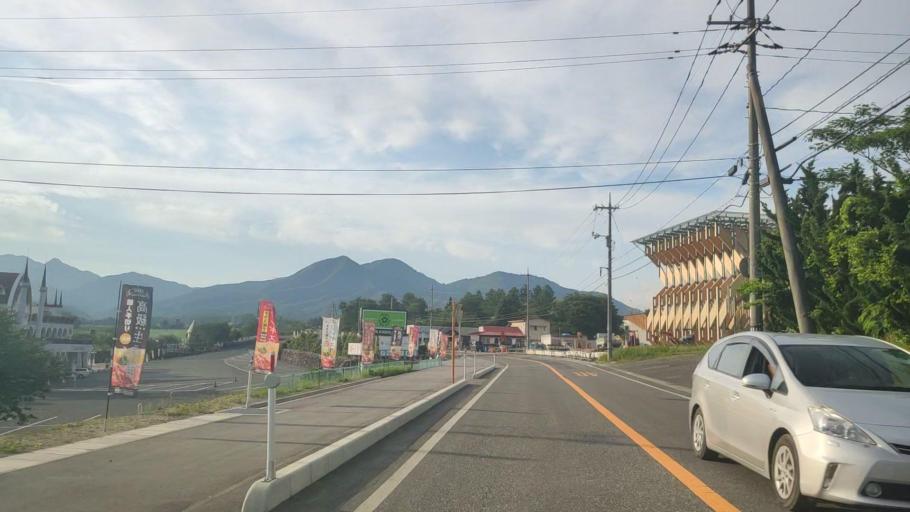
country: JP
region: Tottori
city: Kurayoshi
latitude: 35.2903
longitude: 133.6365
